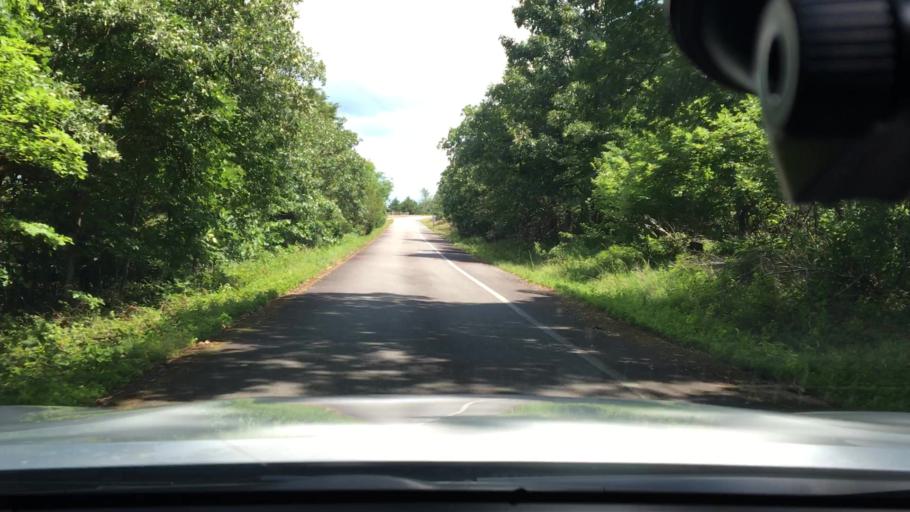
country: US
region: Arkansas
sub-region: Logan County
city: Paris
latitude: 35.1704
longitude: -93.6478
